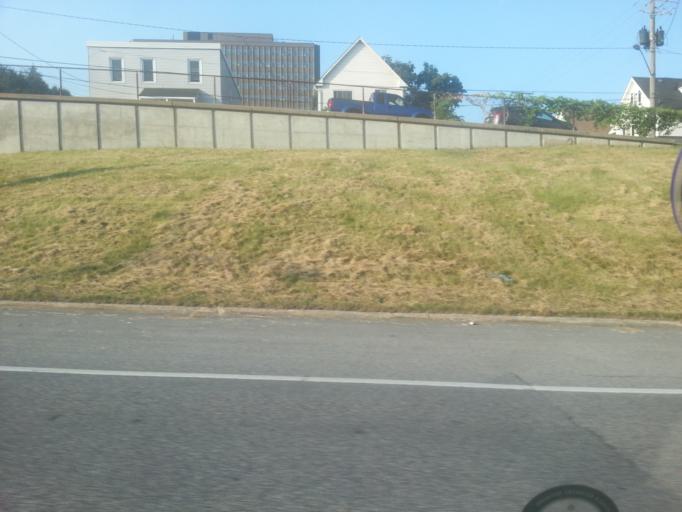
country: CA
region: Ontario
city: Ottawa
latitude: 45.4385
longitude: -75.7093
